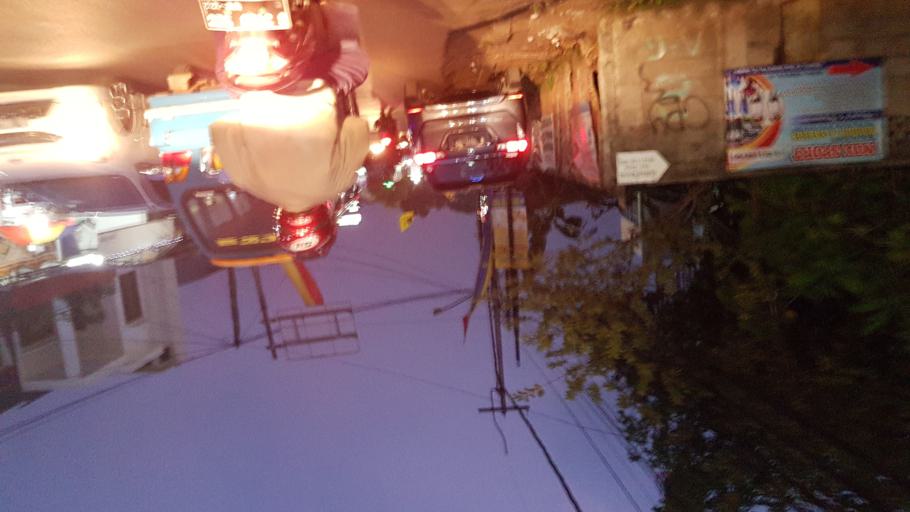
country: ID
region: West Java
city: Pamulang
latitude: -6.3395
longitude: 106.7937
